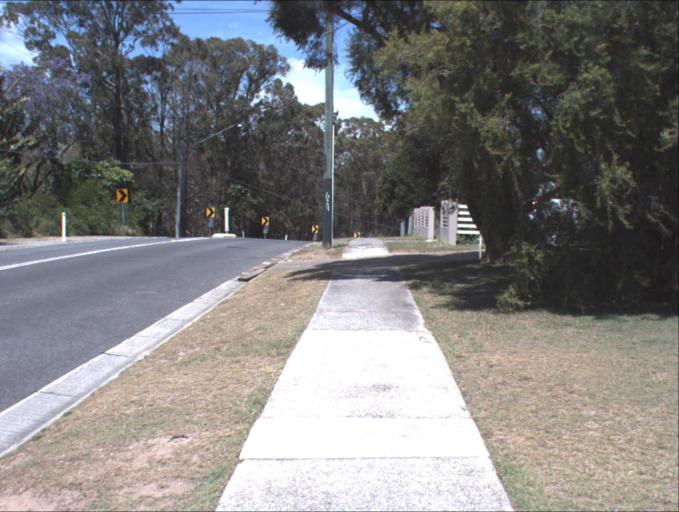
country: AU
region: Queensland
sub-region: Logan
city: Rochedale South
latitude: -27.5897
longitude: 153.1395
